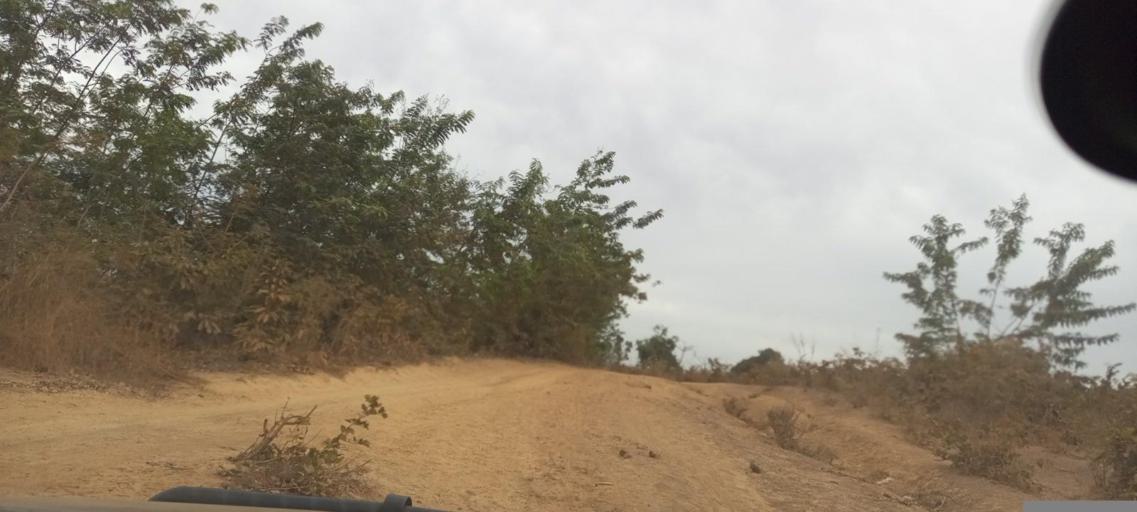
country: ML
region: Koulikoro
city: Kati
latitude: 12.7903
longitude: -8.2556
